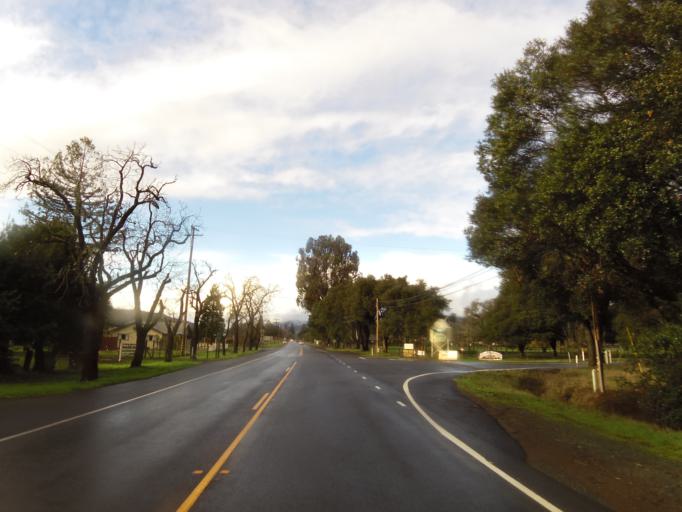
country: US
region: California
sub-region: Mendocino County
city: Boonville
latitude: 38.9988
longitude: -123.3580
